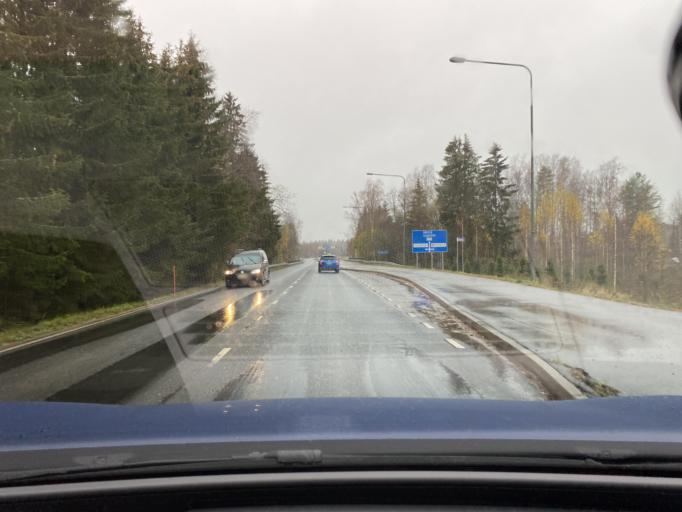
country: FI
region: Varsinais-Suomi
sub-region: Loimaa
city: Loimaa
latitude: 60.8584
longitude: 23.0327
